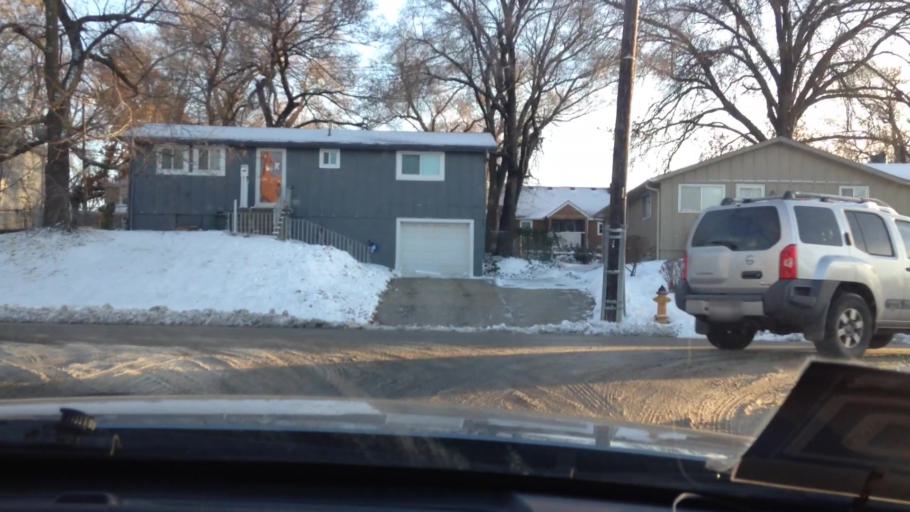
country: US
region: Kansas
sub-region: Johnson County
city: Roeland Park
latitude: 39.0442
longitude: -94.6341
